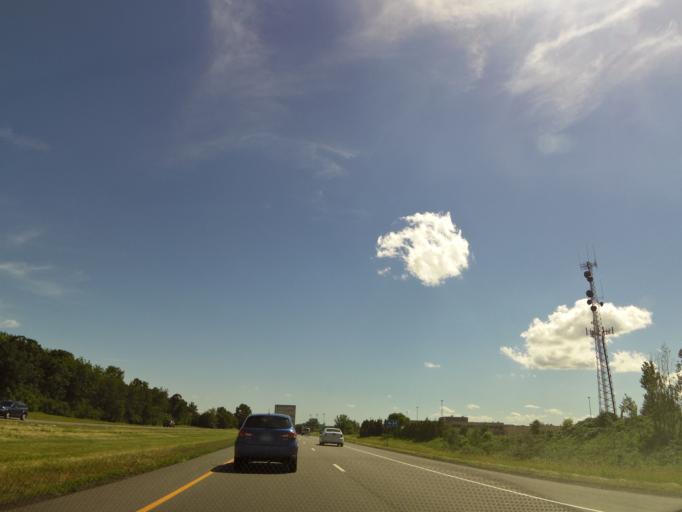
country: US
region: Minnesota
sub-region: Stearns County
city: Waite Park
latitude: 45.5784
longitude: -94.2031
